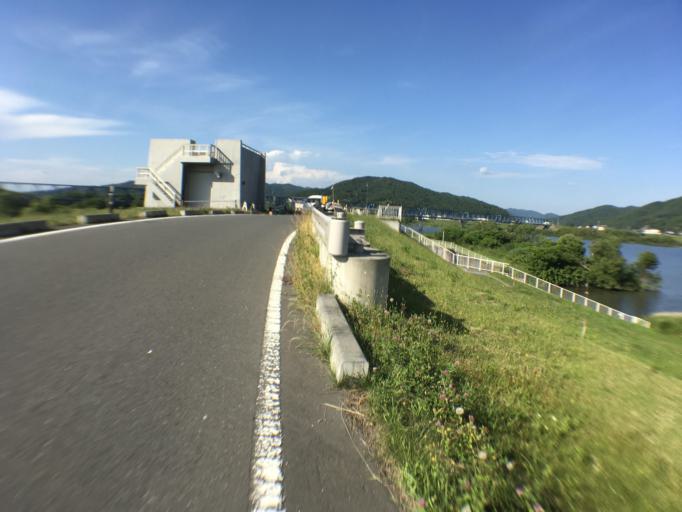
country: JP
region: Miyagi
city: Wakuya
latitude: 38.6064
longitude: 141.2937
